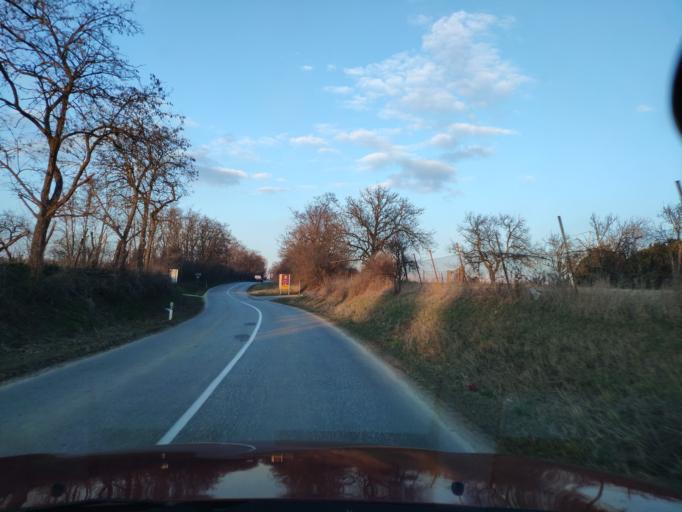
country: SK
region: Nitriansky
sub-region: Okres Nitra
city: Nitra
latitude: 48.2138
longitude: 18.0731
